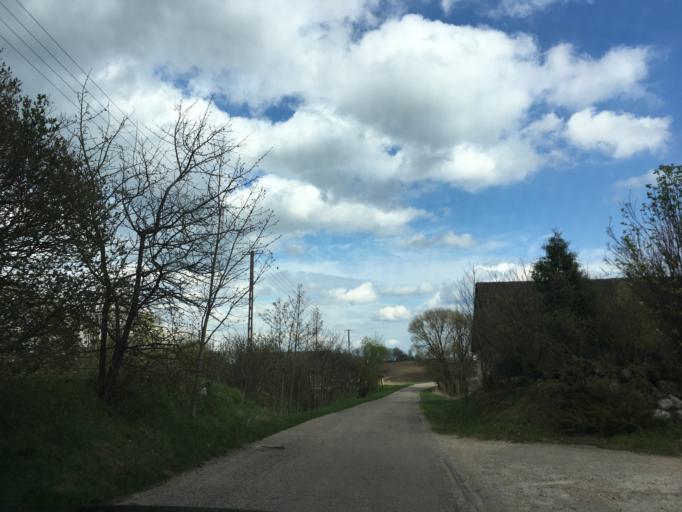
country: PL
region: Podlasie
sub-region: Suwalki
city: Suwalki
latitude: 54.3701
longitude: 22.9170
